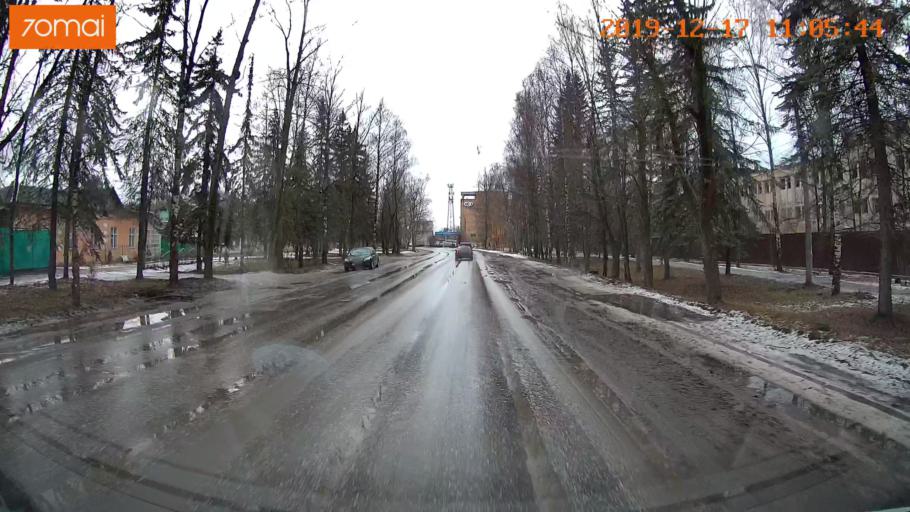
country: RU
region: Vladimir
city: Gus'-Khrustal'nyy
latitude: 55.6193
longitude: 40.6429
